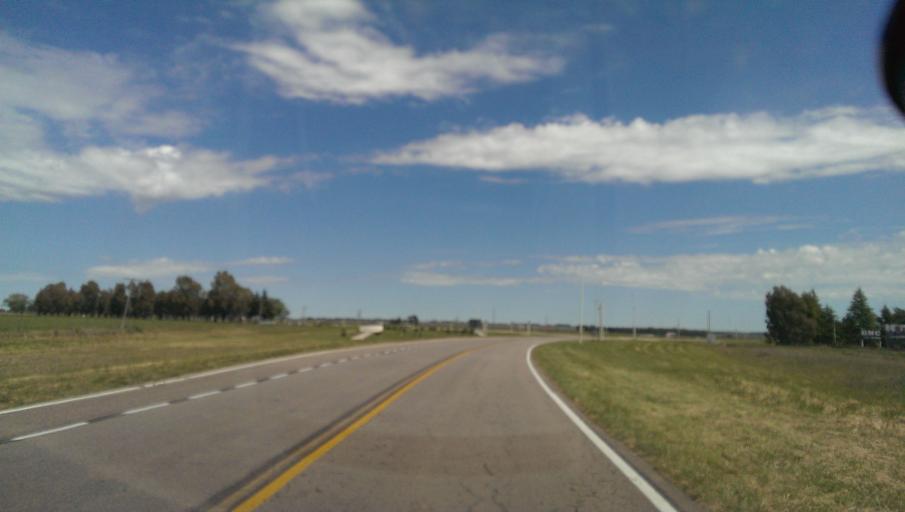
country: AR
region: Buenos Aires
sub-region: Partido de Tornquist
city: Tornquist
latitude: -38.0693
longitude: -62.2189
